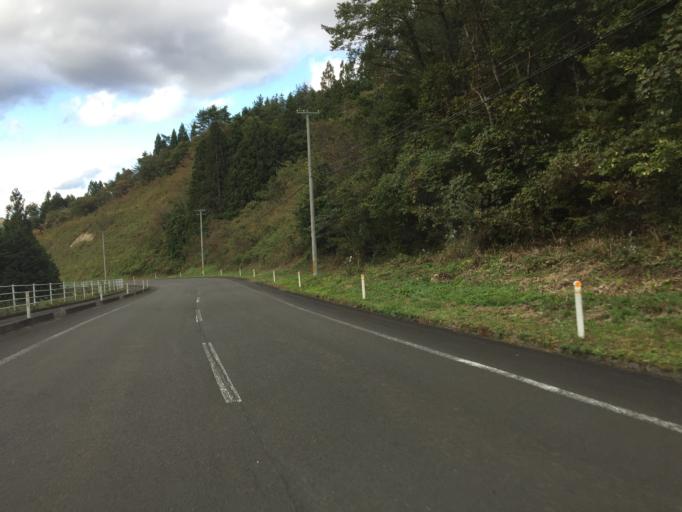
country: JP
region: Miyagi
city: Marumori
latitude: 37.8150
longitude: 140.7339
